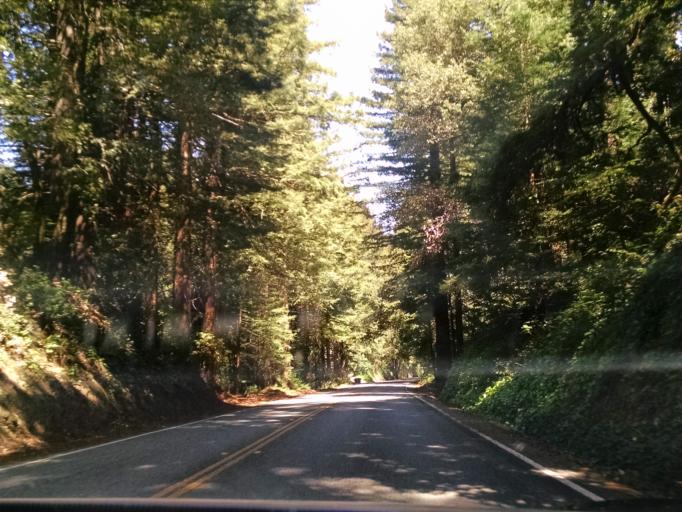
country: US
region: California
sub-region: San Mateo County
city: Portola Valley
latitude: 37.3788
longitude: -122.2627
